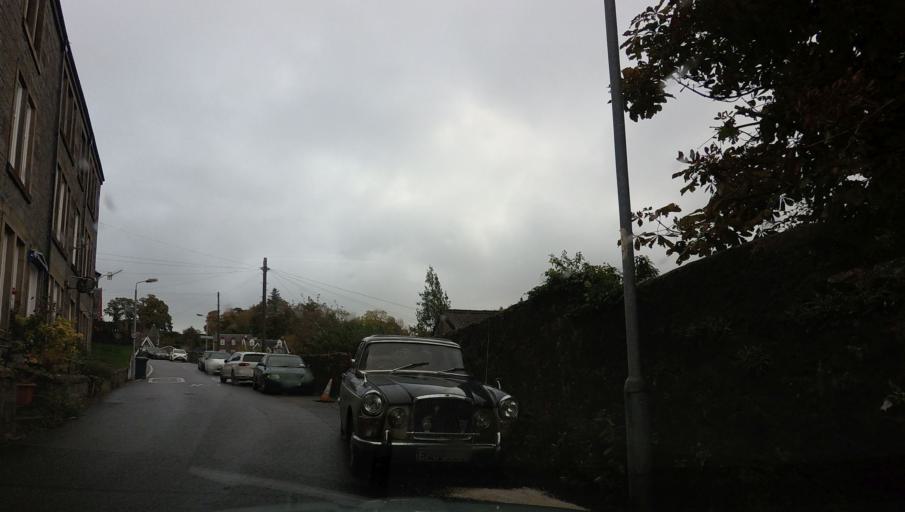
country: GB
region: Scotland
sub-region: Argyll and Bute
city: Oban
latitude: 56.4149
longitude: -5.4697
